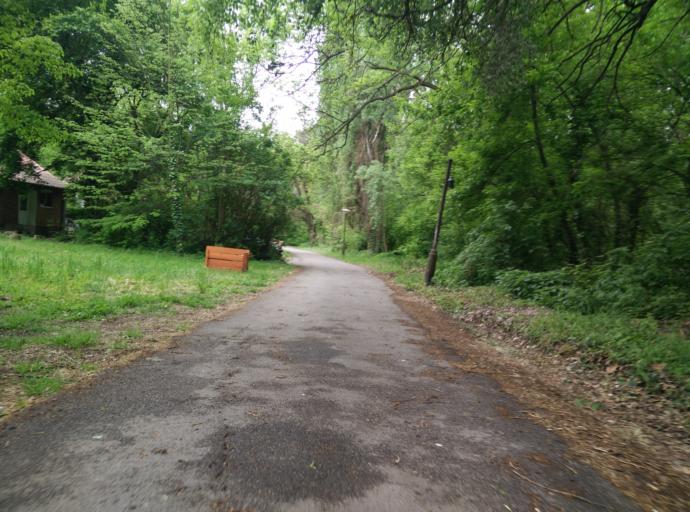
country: HU
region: Pest
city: Fot
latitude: 47.6072
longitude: 19.1904
